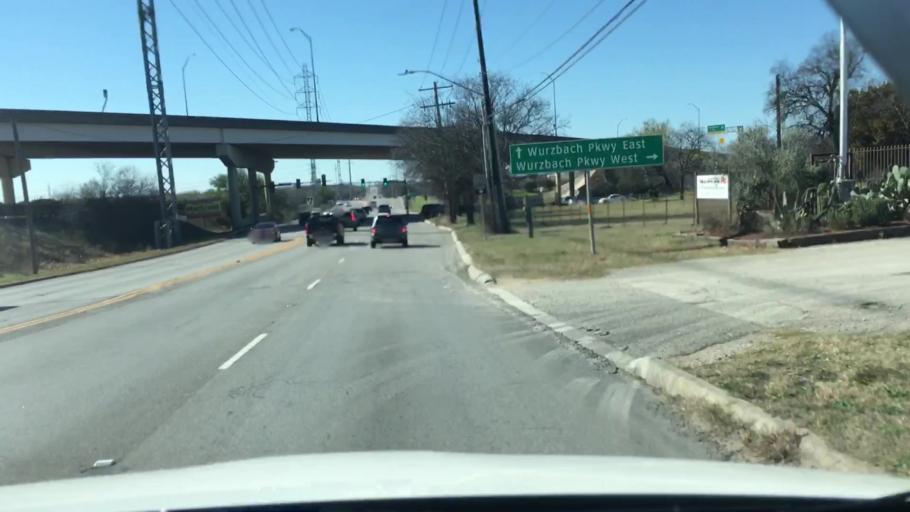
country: US
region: Texas
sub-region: Bexar County
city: Windcrest
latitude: 29.5470
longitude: -98.4348
